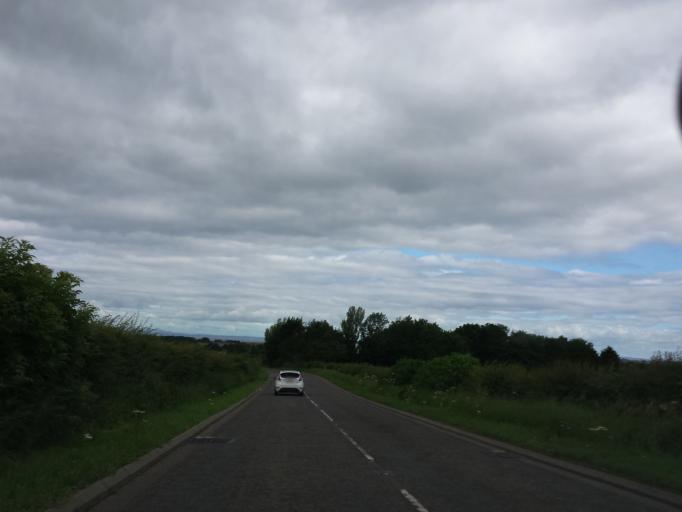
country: GB
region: Scotland
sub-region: East Lothian
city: Gullane
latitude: 55.9891
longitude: -2.8297
